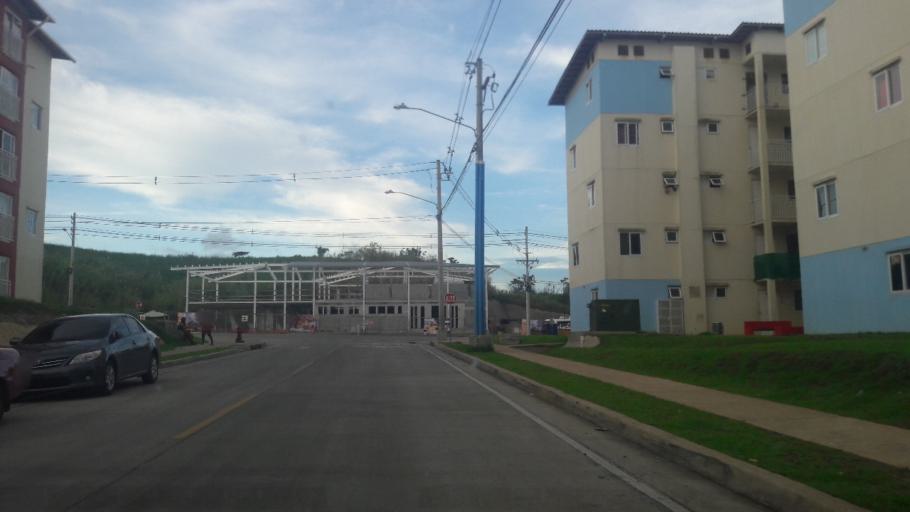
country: PA
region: Colon
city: Cativa
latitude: 9.3648
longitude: -79.8530
